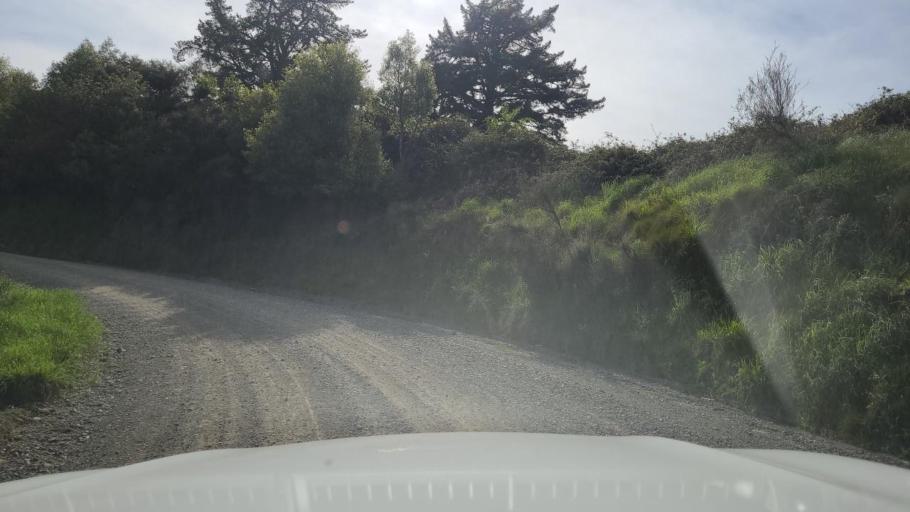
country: NZ
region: Hawke's Bay
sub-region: Napier City
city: Taradale
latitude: -39.3399
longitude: 176.6588
